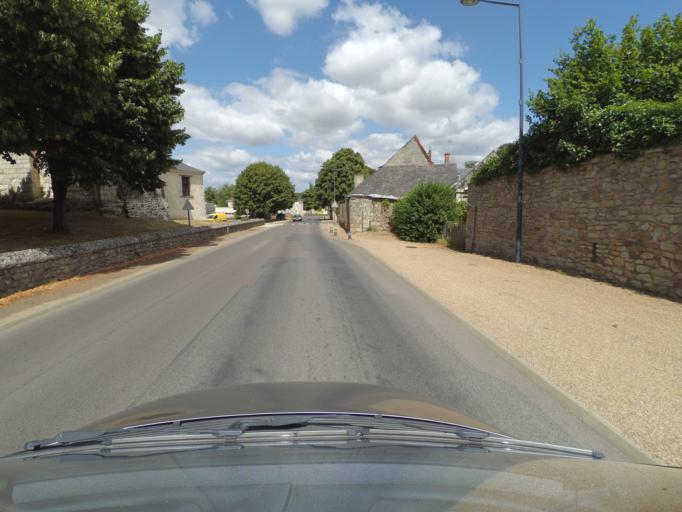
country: FR
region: Pays de la Loire
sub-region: Departement de Maine-et-Loire
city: Gennes
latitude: 47.3373
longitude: -0.2315
